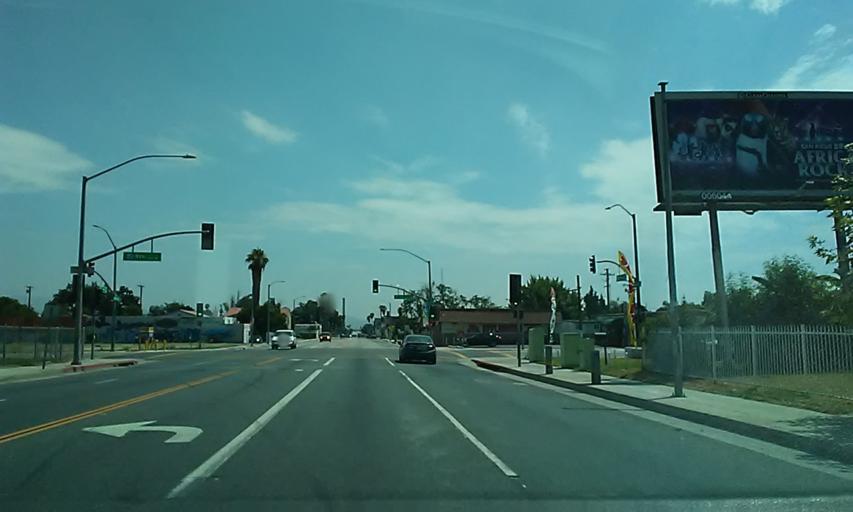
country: US
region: California
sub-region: San Bernardino County
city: San Bernardino
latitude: 34.1163
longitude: -117.3139
